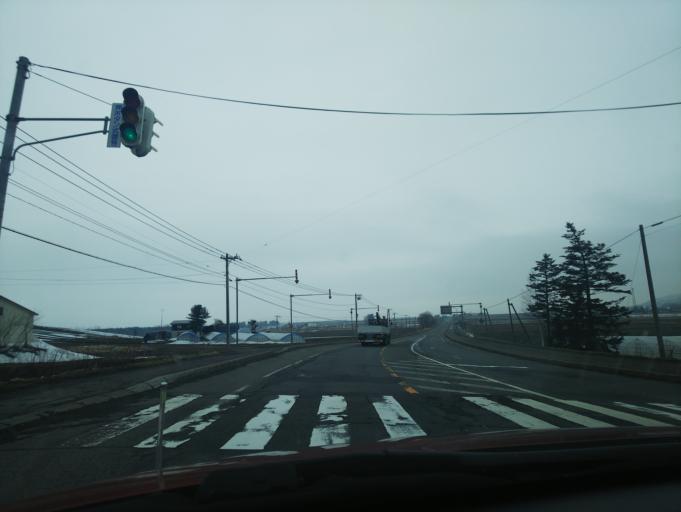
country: JP
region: Hokkaido
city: Nayoro
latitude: 44.0638
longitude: 142.3999
